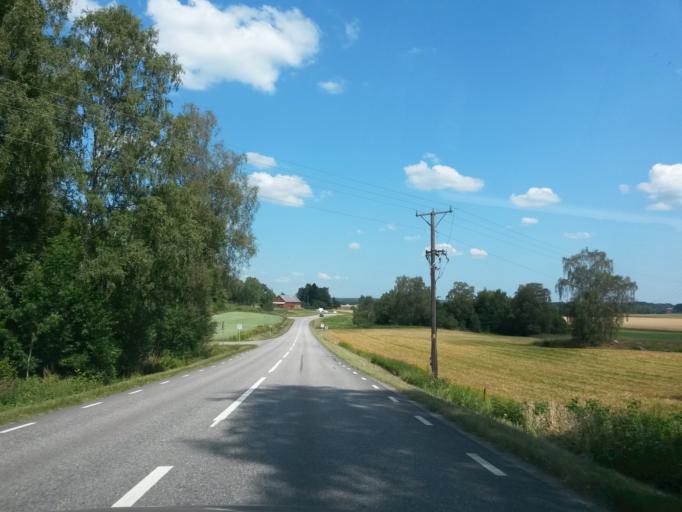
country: SE
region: Vaestra Goetaland
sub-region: Vargarda Kommun
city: Vargarda
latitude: 58.0561
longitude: 12.9009
